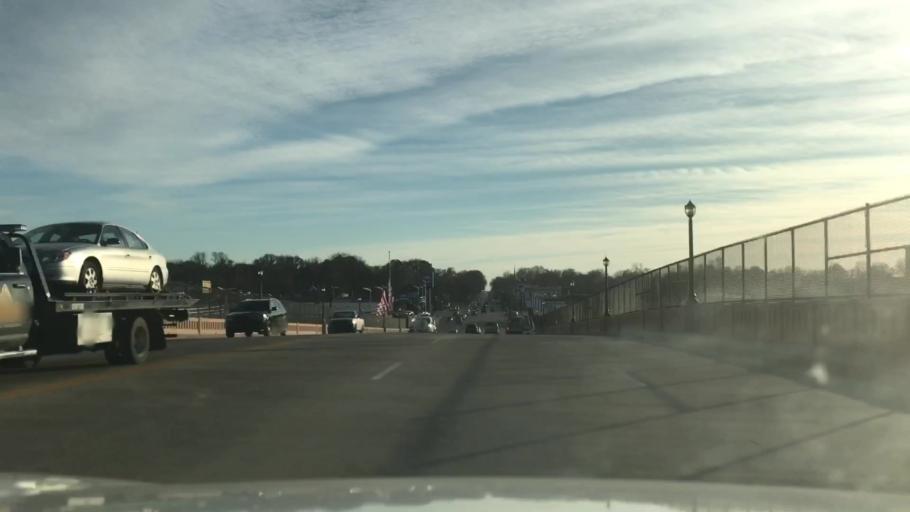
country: US
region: Missouri
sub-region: Saint Louis County
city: Richmond Heights
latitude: 38.6159
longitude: -90.2672
